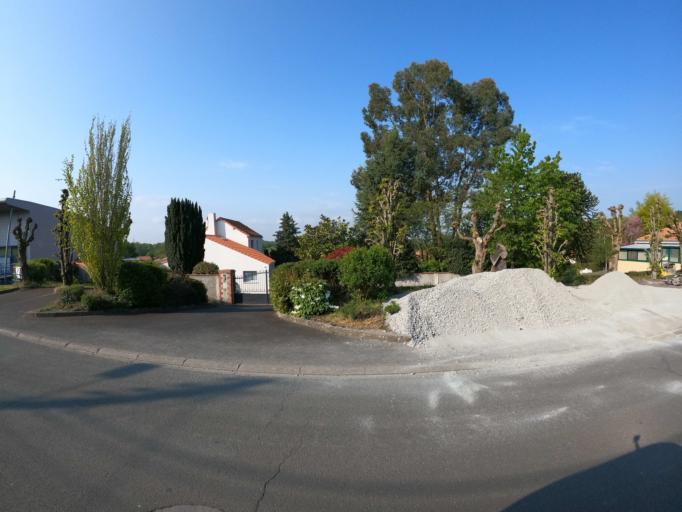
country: FR
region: Pays de la Loire
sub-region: Departement de Maine-et-Loire
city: La Seguiniere
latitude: 47.0639
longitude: -0.9433
